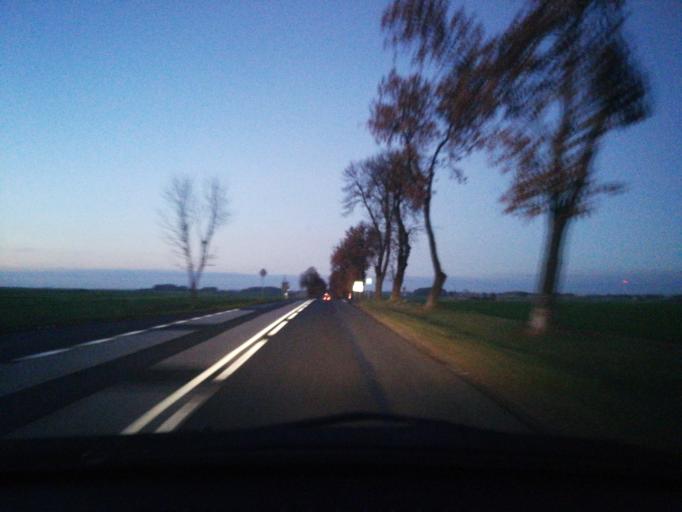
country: PL
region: Lodz Voivodeship
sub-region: Powiat brzezinski
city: Jezow
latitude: 51.8239
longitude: 19.9672
